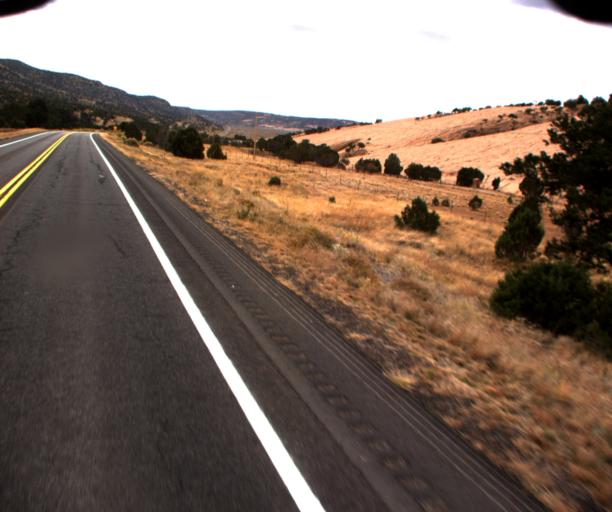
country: US
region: Arizona
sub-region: Navajo County
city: Kayenta
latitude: 36.6437
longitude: -110.4358
